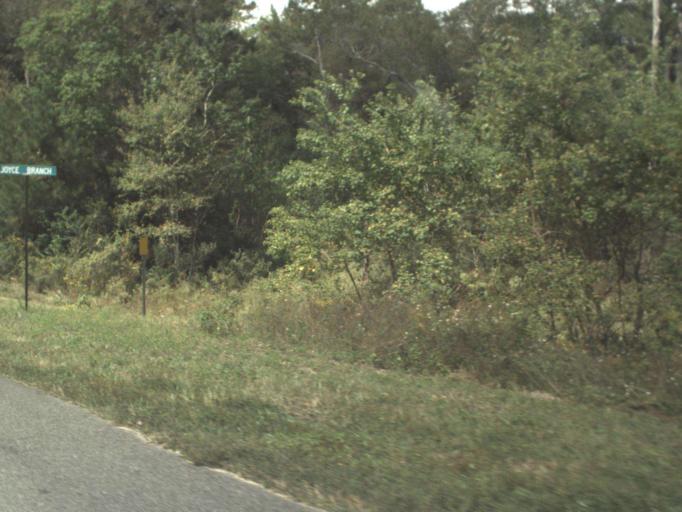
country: US
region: Florida
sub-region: Walton County
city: Freeport
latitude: 30.4785
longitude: -86.0649
